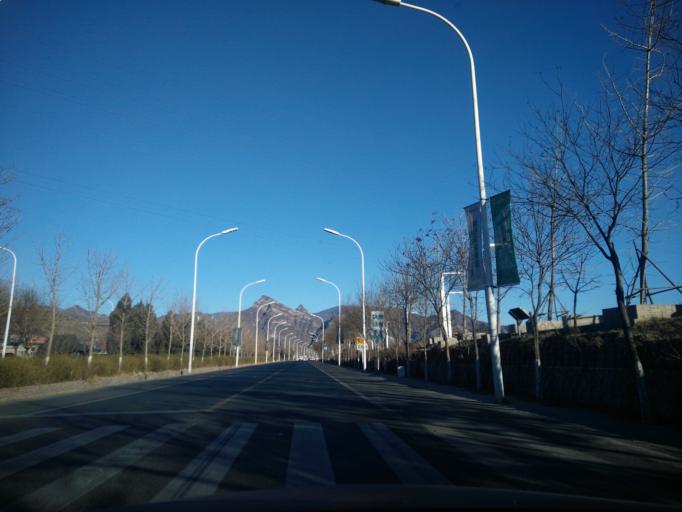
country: CN
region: Beijing
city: Junzhuang
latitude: 39.9768
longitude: 116.0845
